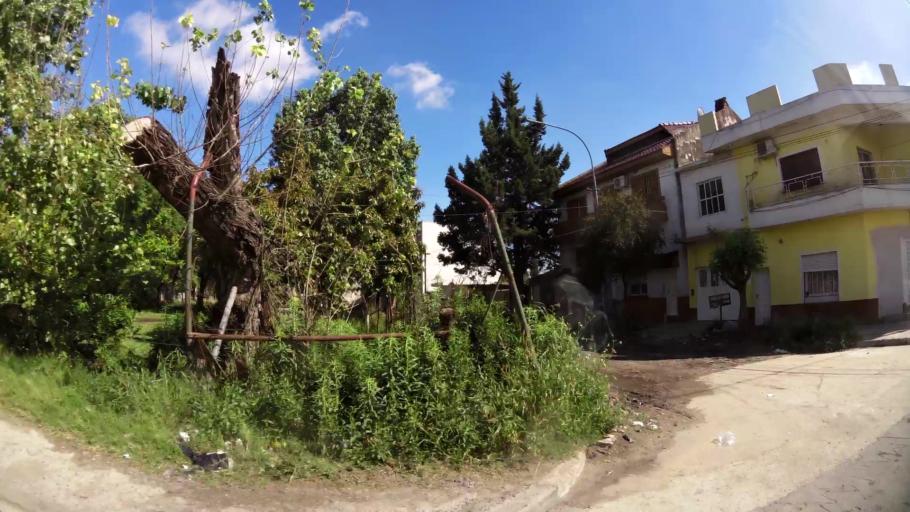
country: AR
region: Buenos Aires
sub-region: Partido de Lanus
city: Lanus
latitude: -34.6717
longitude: -58.4232
